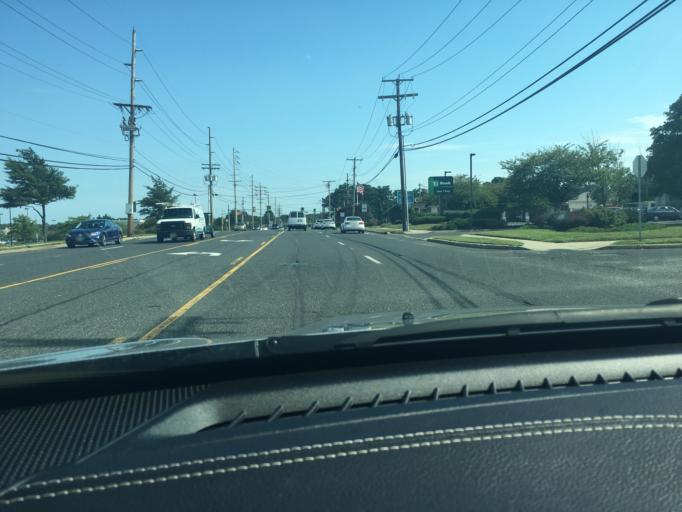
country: US
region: New Jersey
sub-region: Ocean County
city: Leisure Village East
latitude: 40.0570
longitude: -74.1435
